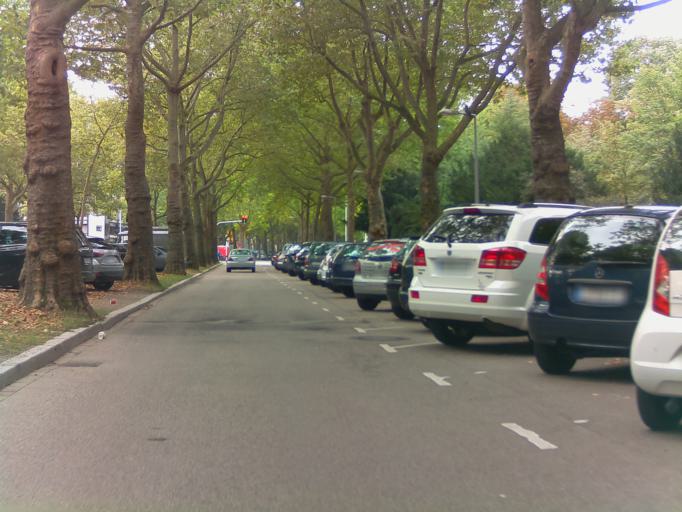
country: DE
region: Baden-Wuerttemberg
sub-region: Karlsruhe Region
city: Mannheim
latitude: 49.4861
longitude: 8.4884
